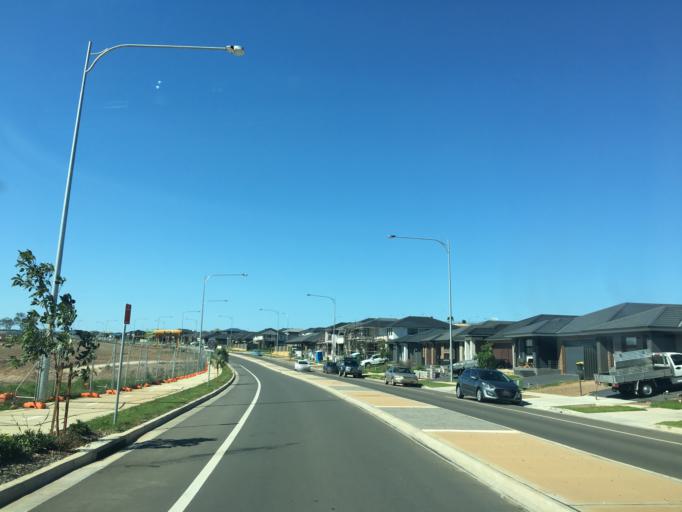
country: AU
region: New South Wales
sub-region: Campbelltown Municipality
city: Denham Court
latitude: -33.9965
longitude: 150.7933
